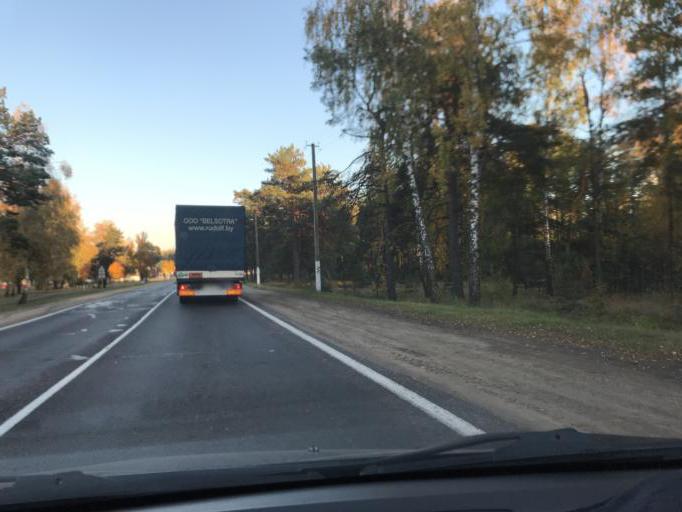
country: BY
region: Minsk
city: Staryya Darohi
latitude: 53.0326
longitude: 28.2573
